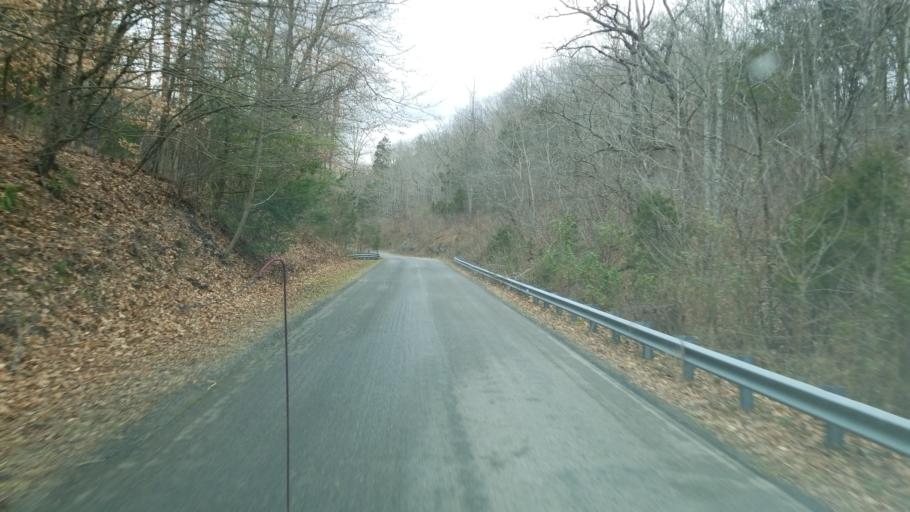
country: US
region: Virginia
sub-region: Giles County
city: Pearisburg
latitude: 37.2321
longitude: -80.7003
